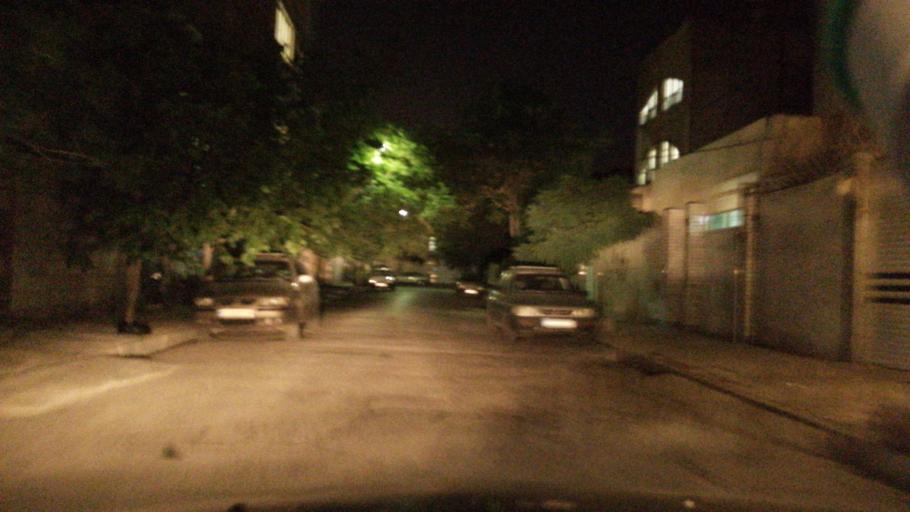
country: IR
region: Razavi Khorasan
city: Mashhad
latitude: 36.3082
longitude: 59.6028
